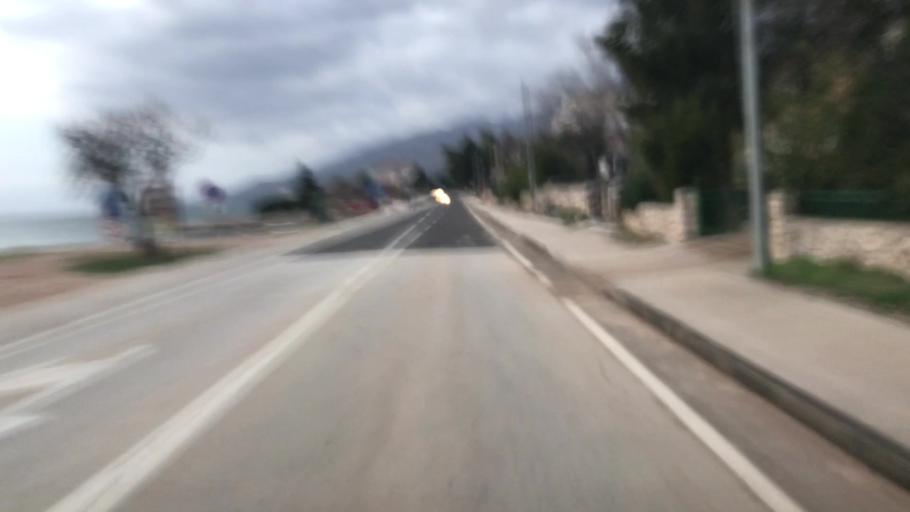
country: HR
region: Zadarska
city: Starigrad
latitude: 44.2893
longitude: 15.4448
